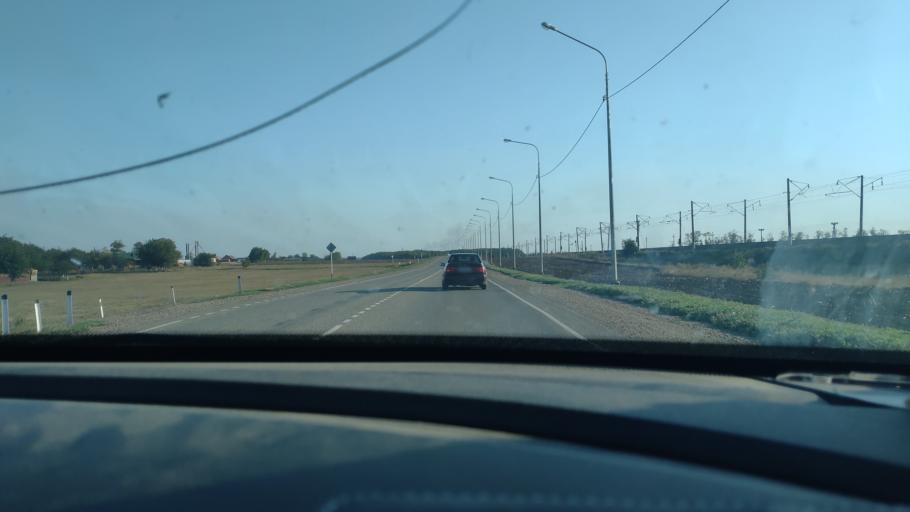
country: RU
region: Krasnodarskiy
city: Novominskaya
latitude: 46.3128
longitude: 38.9305
